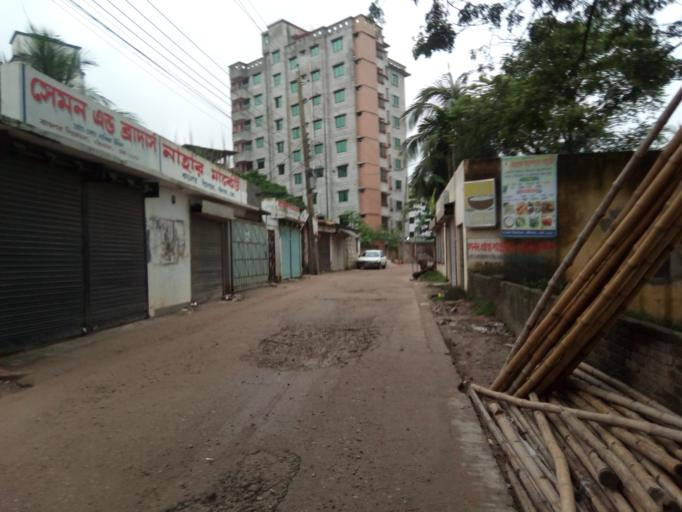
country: BD
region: Dhaka
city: Tungi
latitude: 23.8485
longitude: 90.4234
